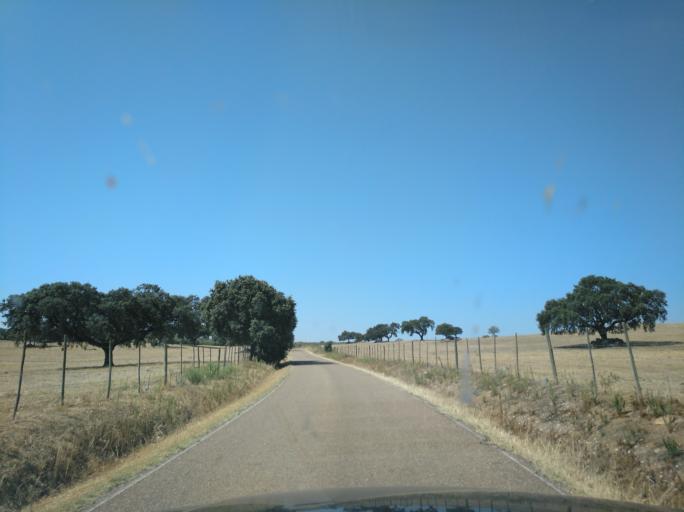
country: PT
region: Portalegre
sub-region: Campo Maior
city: Campo Maior
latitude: 39.0449
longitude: -7.0235
